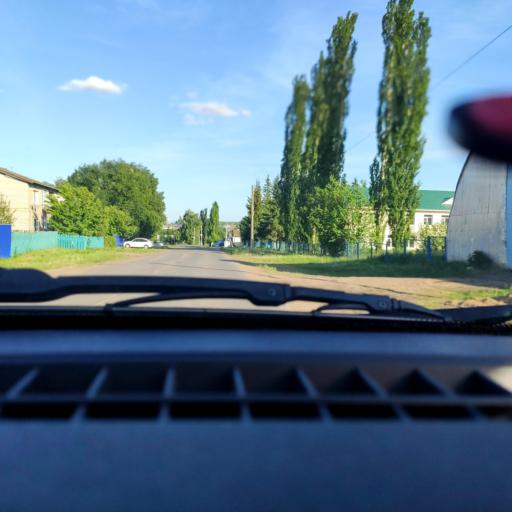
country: RU
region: Bashkortostan
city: Tolbazy
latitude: 54.2922
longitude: 55.8133
